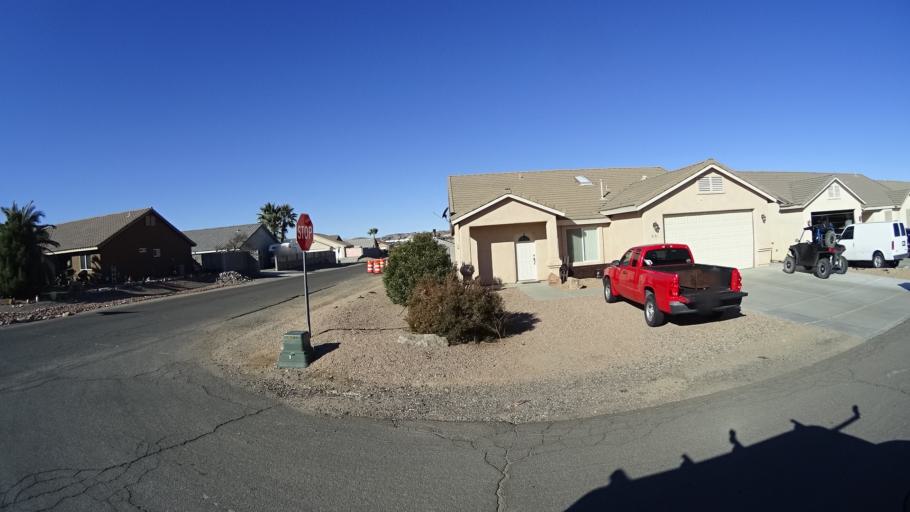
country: US
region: Arizona
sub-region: Mohave County
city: Kingman
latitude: 35.2140
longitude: -114.0068
